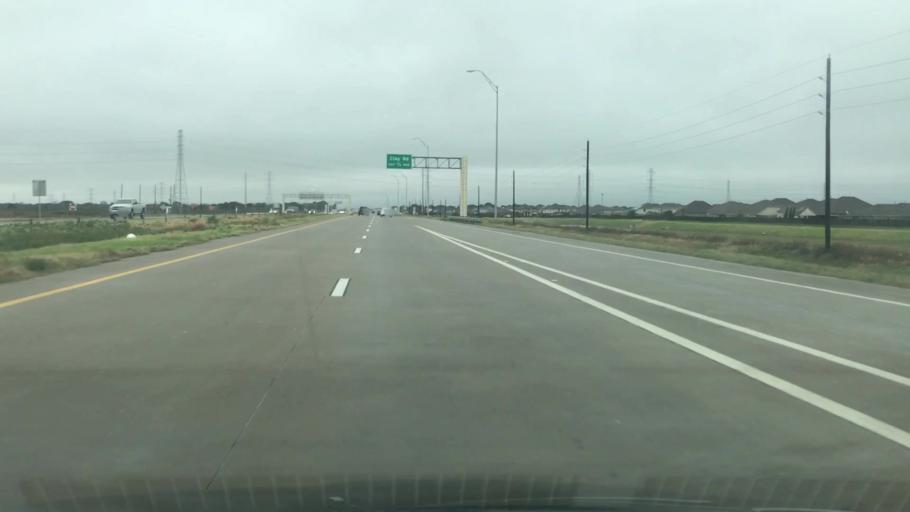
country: US
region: Texas
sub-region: Harris County
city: Katy
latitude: 29.8214
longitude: -95.7679
